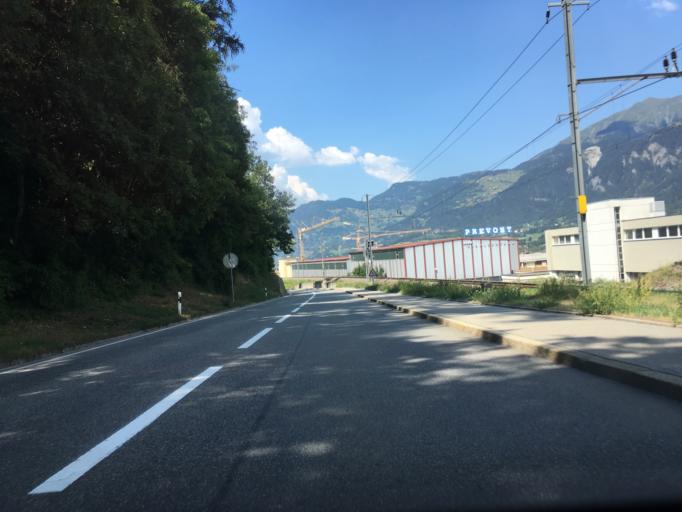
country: CH
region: Grisons
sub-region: Hinterrhein District
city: Thusis
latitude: 46.7032
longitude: 9.4396
